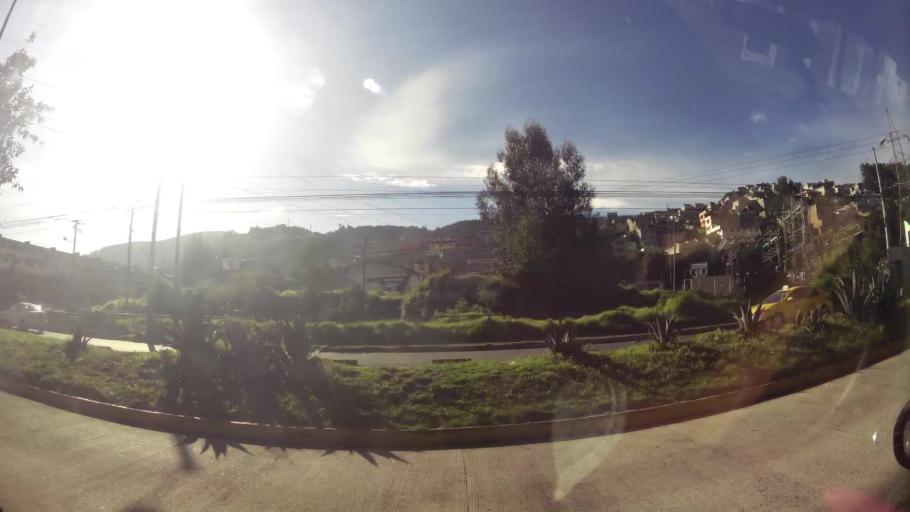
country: EC
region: Pichincha
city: Quito
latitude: -0.2756
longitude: -78.5301
